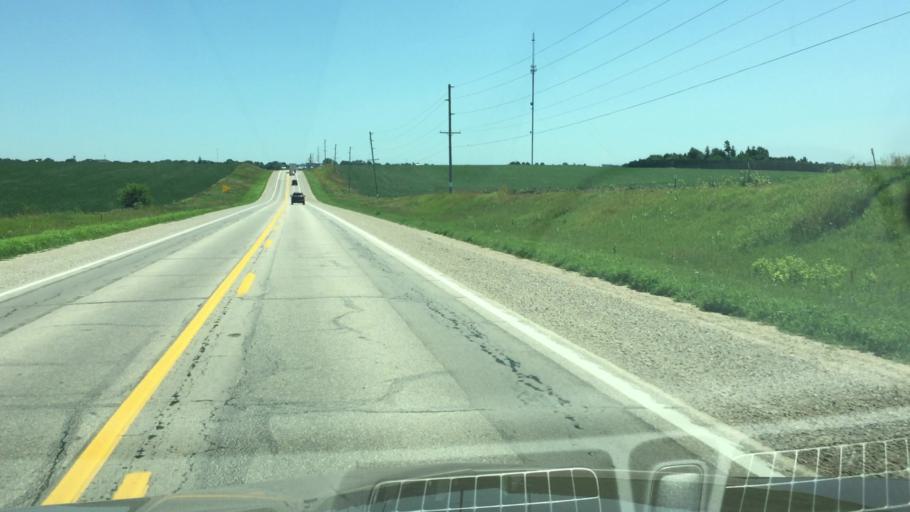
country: US
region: Iowa
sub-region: Cedar County
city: Mechanicsville
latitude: 41.8885
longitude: -91.1815
